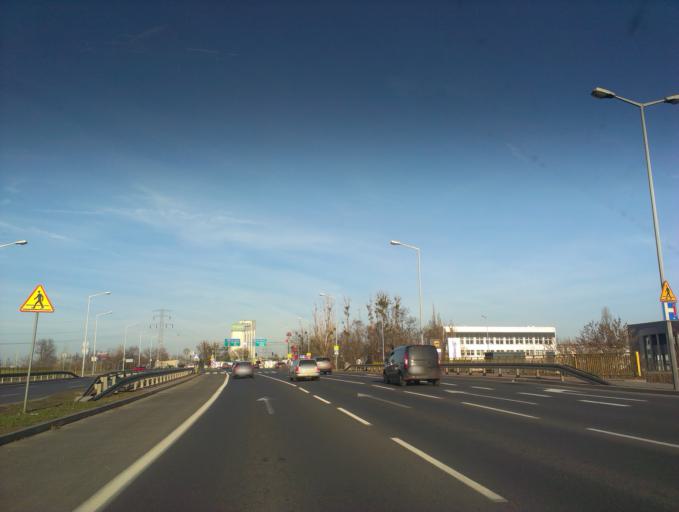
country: PL
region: Greater Poland Voivodeship
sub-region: Poznan
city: Poznan
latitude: 52.4252
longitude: 16.9657
